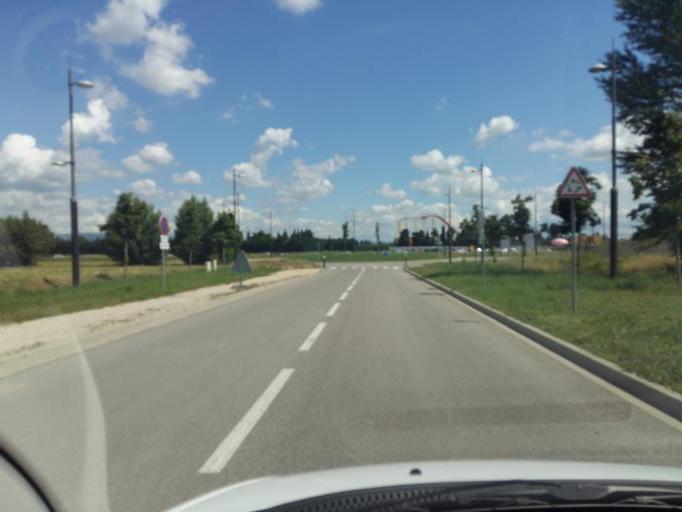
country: FR
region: Provence-Alpes-Cote d'Azur
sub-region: Departement du Vaucluse
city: Althen-des-Paluds
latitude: 44.0250
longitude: 4.9699
